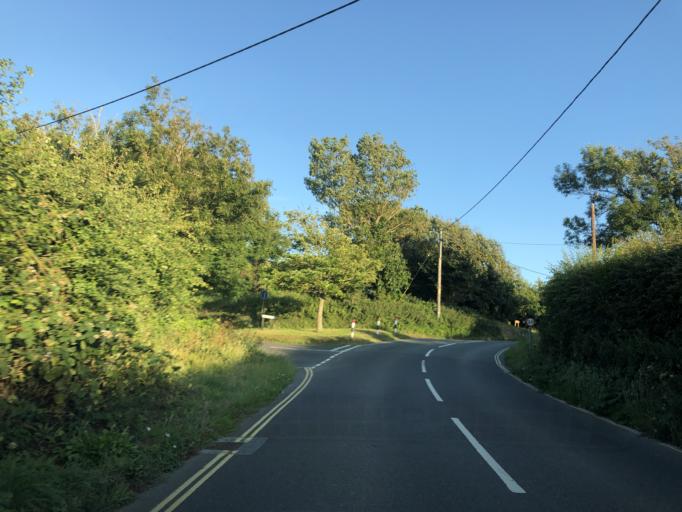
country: GB
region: England
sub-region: Isle of Wight
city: Chale
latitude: 50.5986
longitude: -1.3168
